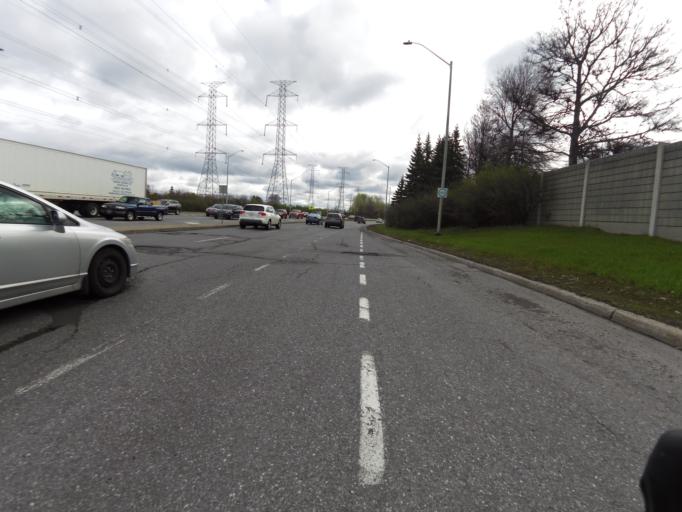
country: CA
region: Ontario
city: Bells Corners
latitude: 45.3290
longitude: -75.7483
